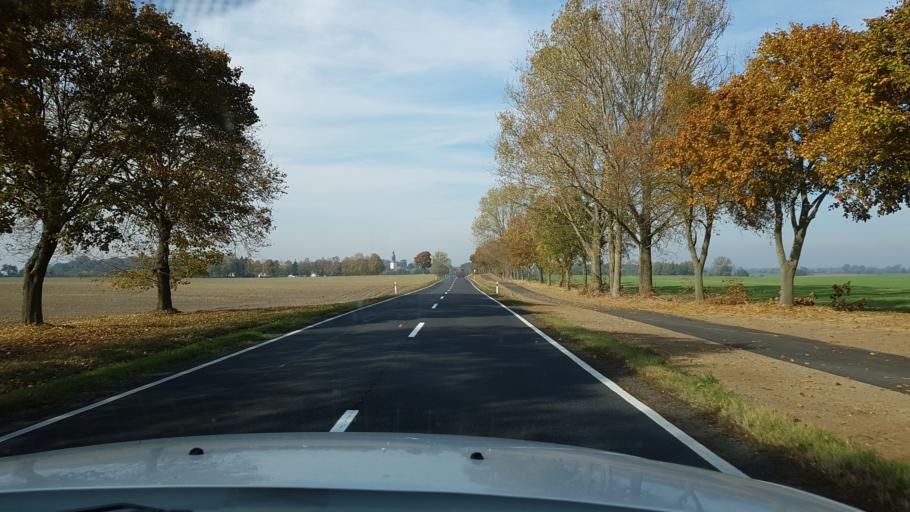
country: PL
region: West Pomeranian Voivodeship
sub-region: Powiat mysliborski
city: Mysliborz
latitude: 52.9426
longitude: 14.8056
